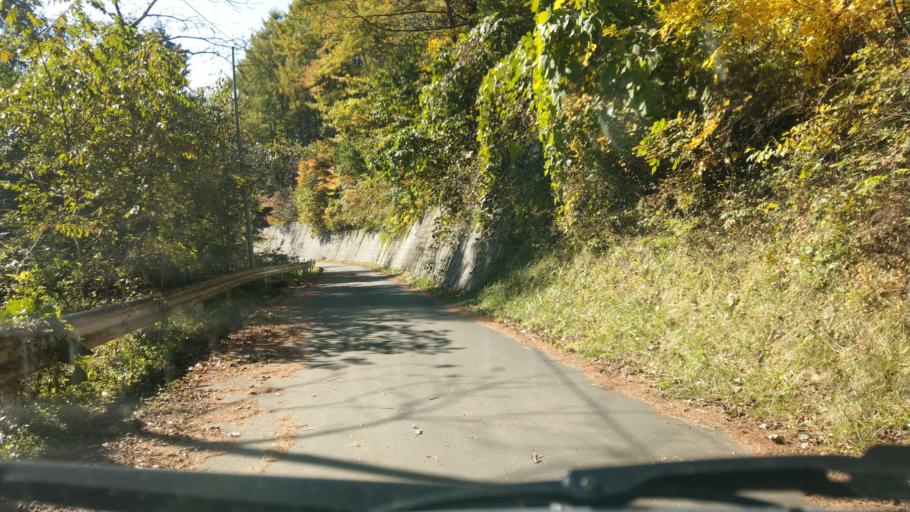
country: JP
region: Nagano
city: Komoro
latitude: 36.3767
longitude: 138.4188
